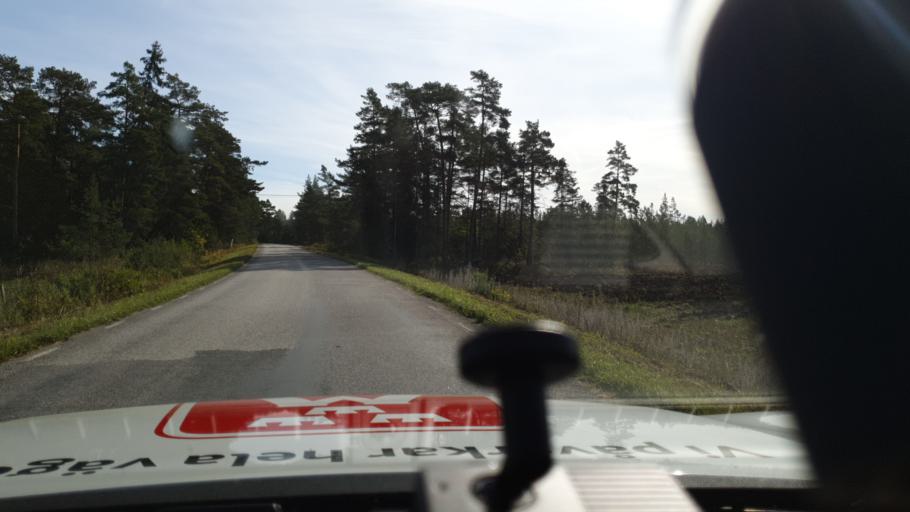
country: SE
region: Gotland
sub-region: Gotland
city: Slite
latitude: 57.8548
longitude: 18.7260
